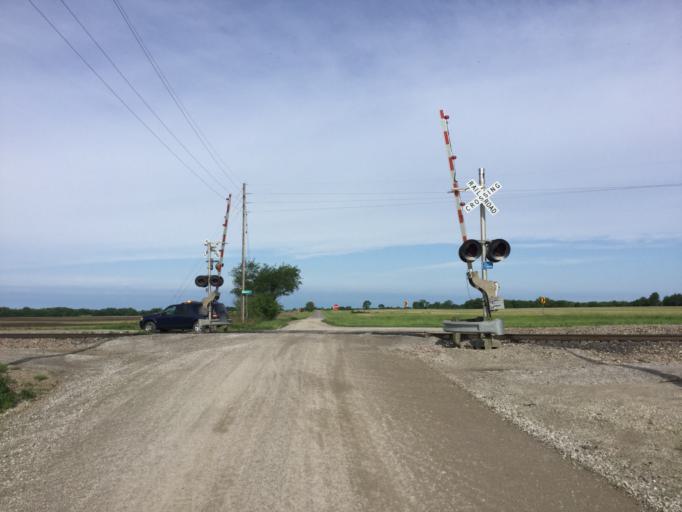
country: US
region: Kansas
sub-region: Linn County
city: Pleasanton
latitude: 38.0414
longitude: -94.6960
